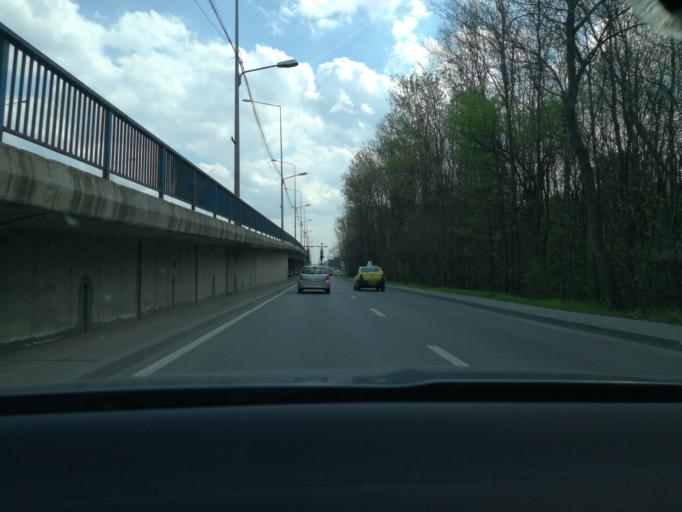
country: RO
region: Ilfov
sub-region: Comuna Otopeni
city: Otopeni
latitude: 44.5158
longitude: 26.0794
